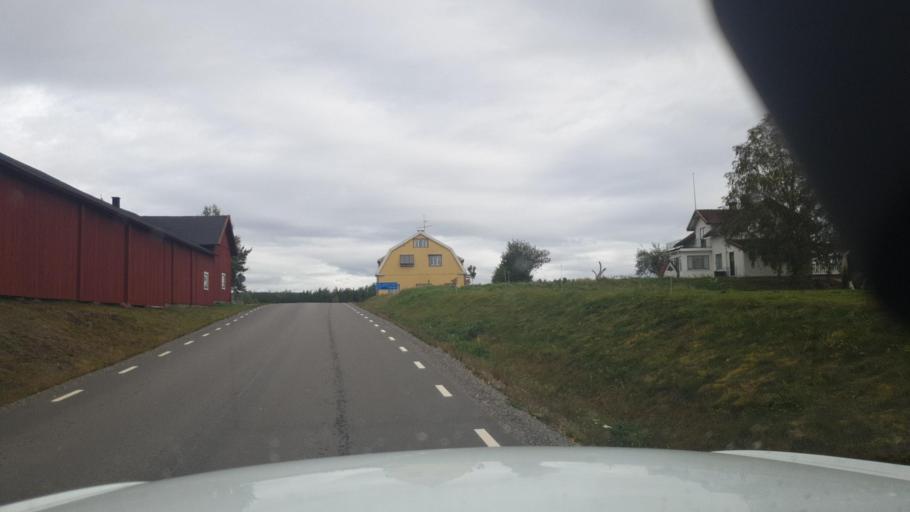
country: SE
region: Vaermland
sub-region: Torsby Kommun
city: Torsby
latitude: 59.9839
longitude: 12.8720
